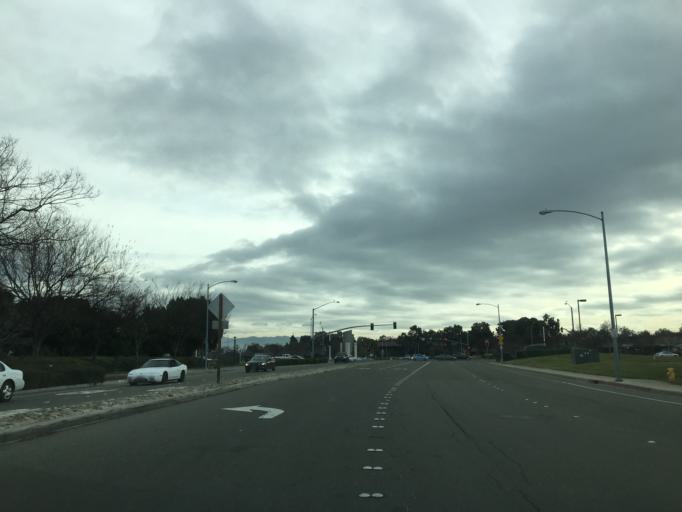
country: US
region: California
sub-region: Santa Clara County
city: Milpitas
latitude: 37.4148
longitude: -121.9181
